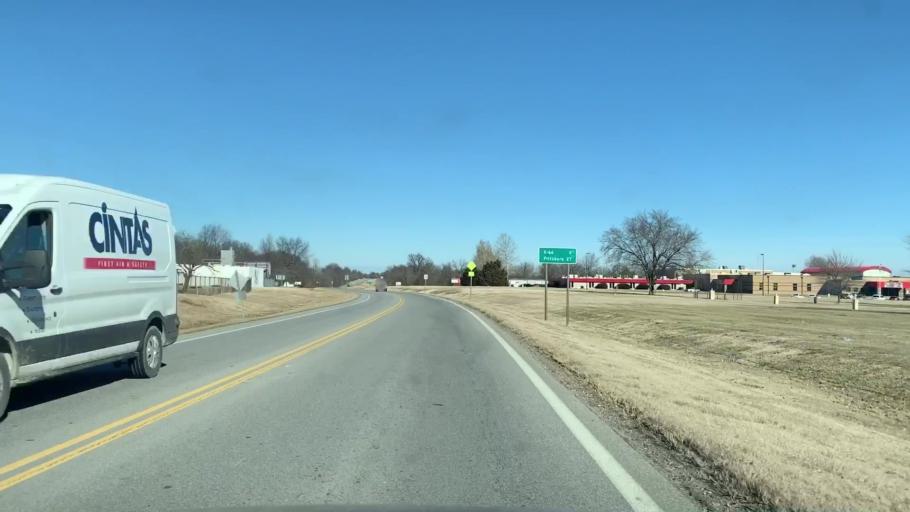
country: US
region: Kansas
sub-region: Cherokee County
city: Baxter Springs
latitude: 37.0343
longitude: -94.7346
